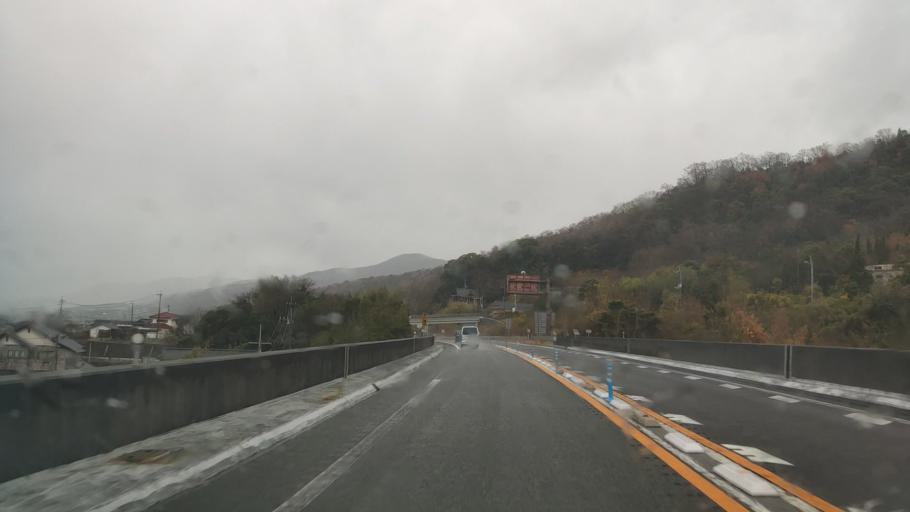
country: JP
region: Tokushima
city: Kamojimacho-jogejima
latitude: 34.1083
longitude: 134.2885
